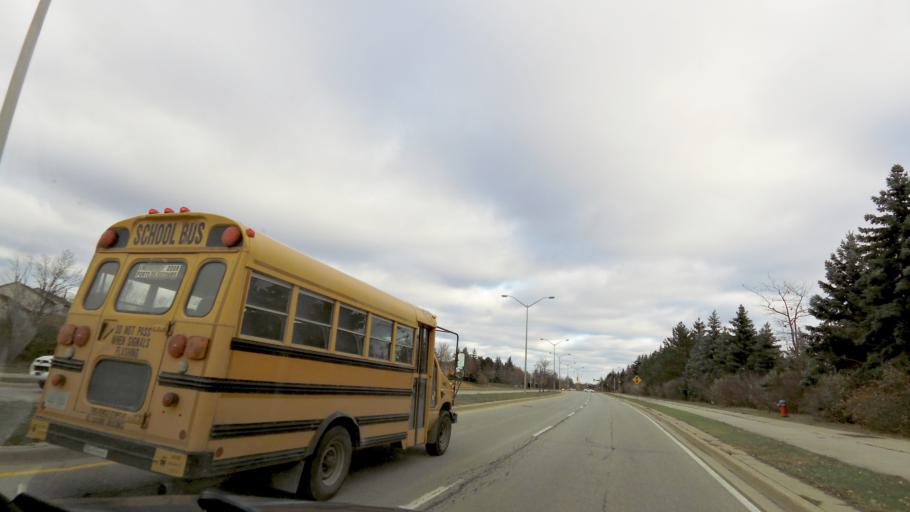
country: CA
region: Ontario
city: Oakville
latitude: 43.4602
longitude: -79.7331
